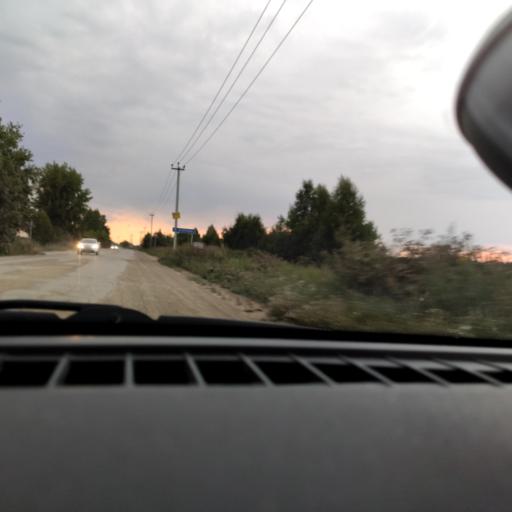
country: RU
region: Perm
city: Kondratovo
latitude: 58.0068
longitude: 56.0384
